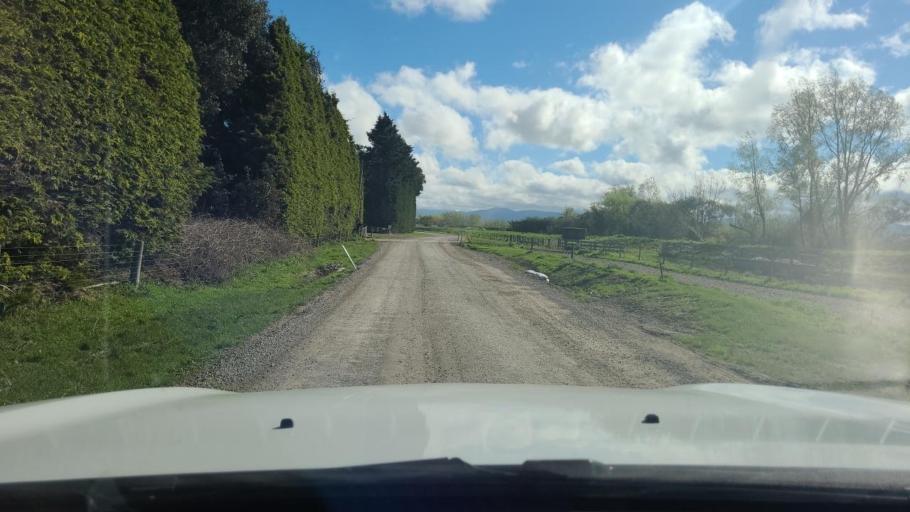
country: NZ
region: Wellington
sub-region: South Wairarapa District
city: Waipawa
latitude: -41.1623
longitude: 175.3579
